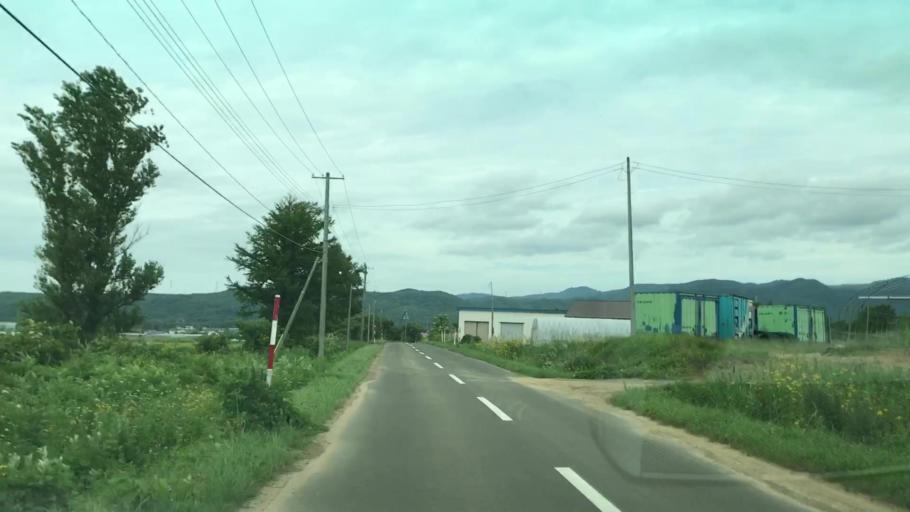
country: JP
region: Hokkaido
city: Iwanai
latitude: 43.0245
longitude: 140.5705
